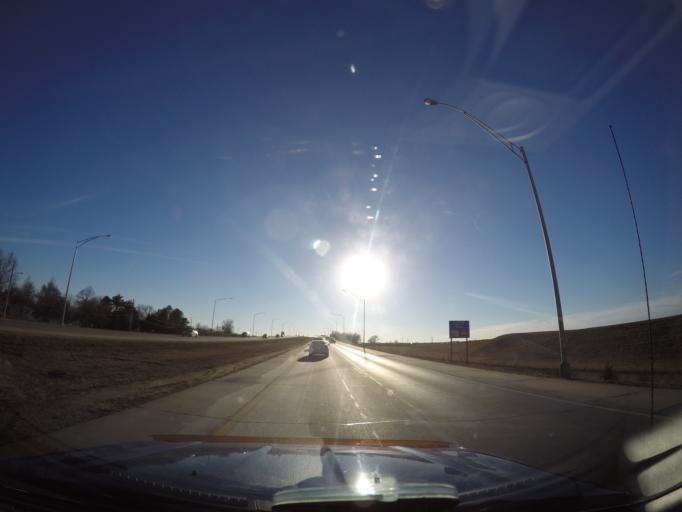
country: US
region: Kansas
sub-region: Sedgwick County
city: Wichita
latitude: 37.7174
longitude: -97.3958
